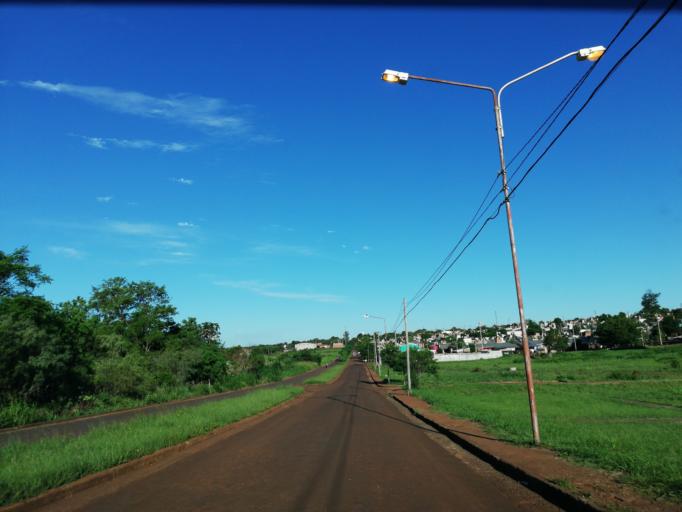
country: AR
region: Misiones
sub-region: Departamento de Capital
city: Posadas
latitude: -27.4352
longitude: -55.9216
